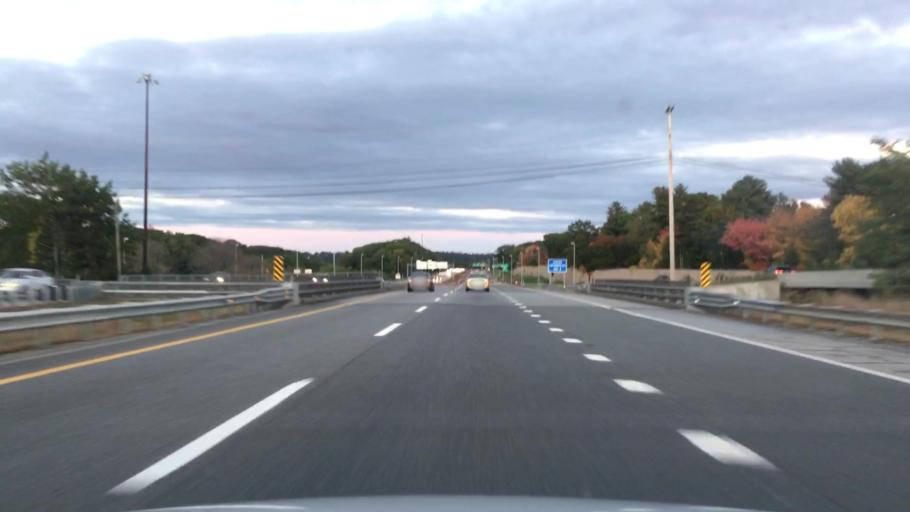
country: US
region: Maine
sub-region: Cumberland County
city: South Portland Gardens
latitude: 43.6310
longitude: -70.3125
